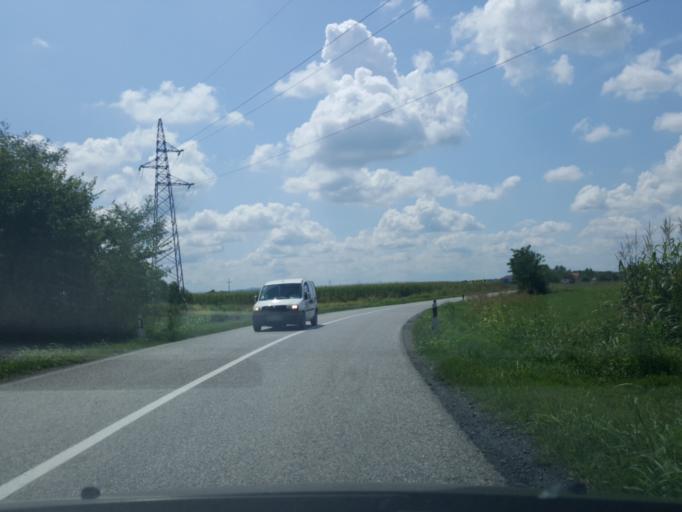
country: RS
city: Metkovic
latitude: 44.8456
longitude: 19.5203
